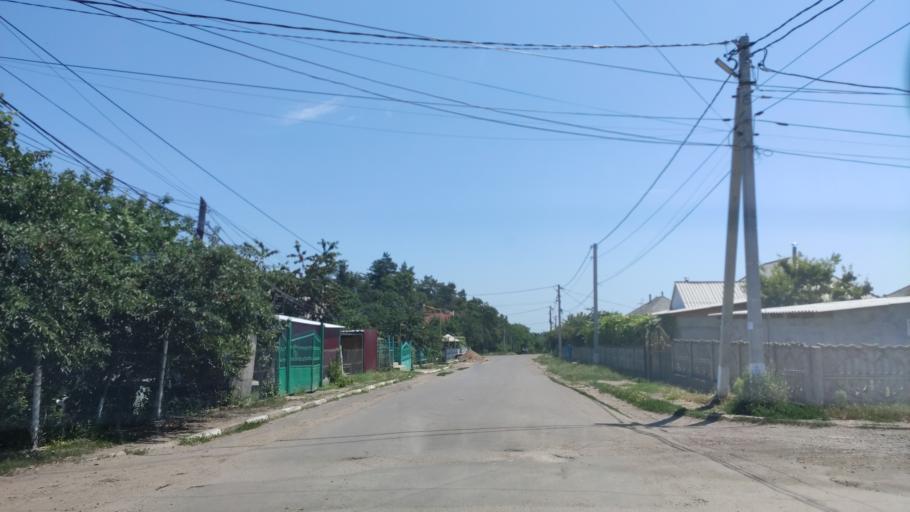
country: MD
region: Raionul Soroca
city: Soroca
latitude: 48.1458
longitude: 28.2881
